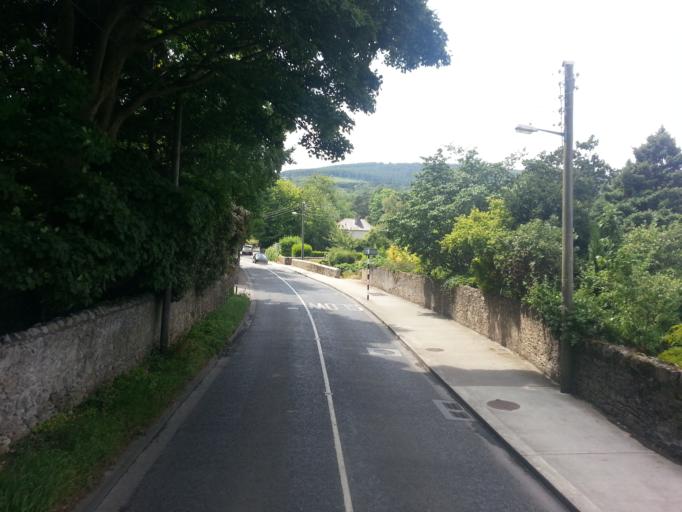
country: IE
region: Leinster
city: Sandyford
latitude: 53.2605
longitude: -6.2107
